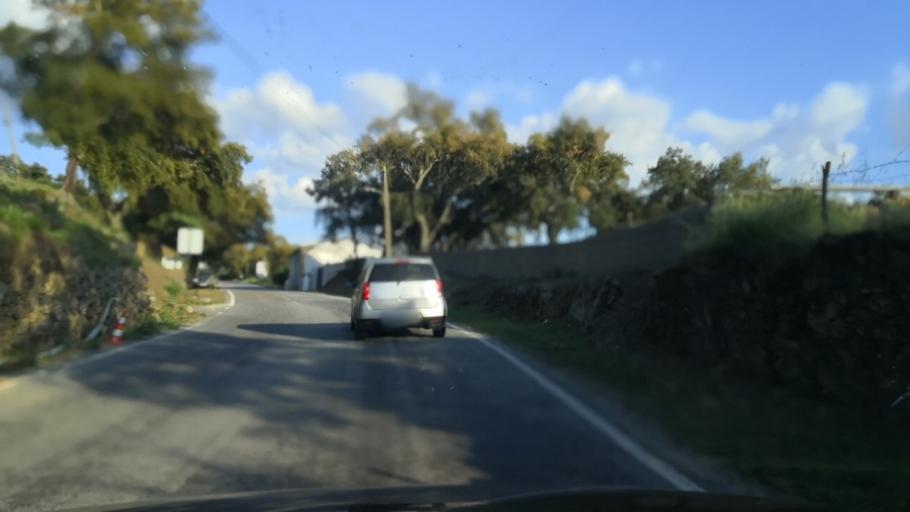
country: PT
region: Portalegre
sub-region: Portalegre
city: Portalegre
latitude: 39.3276
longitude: -7.4255
